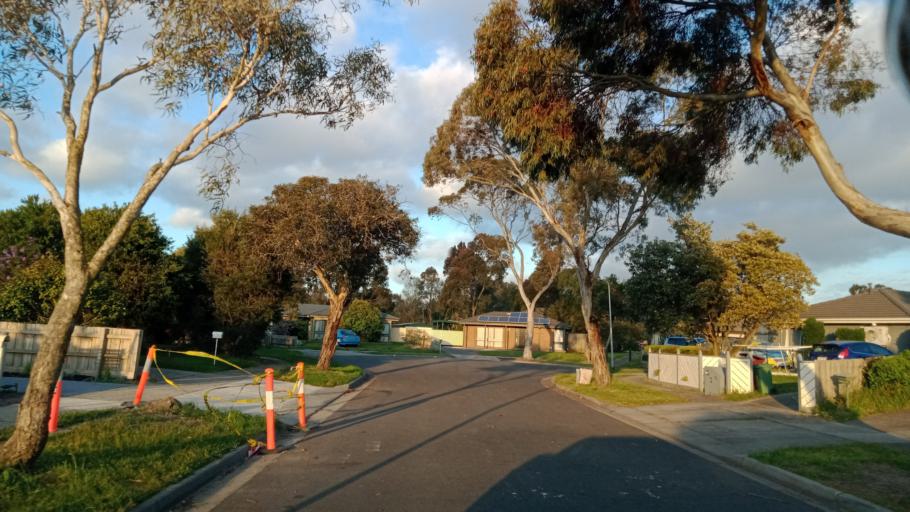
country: AU
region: Victoria
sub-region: Casey
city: Cranbourne North
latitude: -38.0778
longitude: 145.2643
